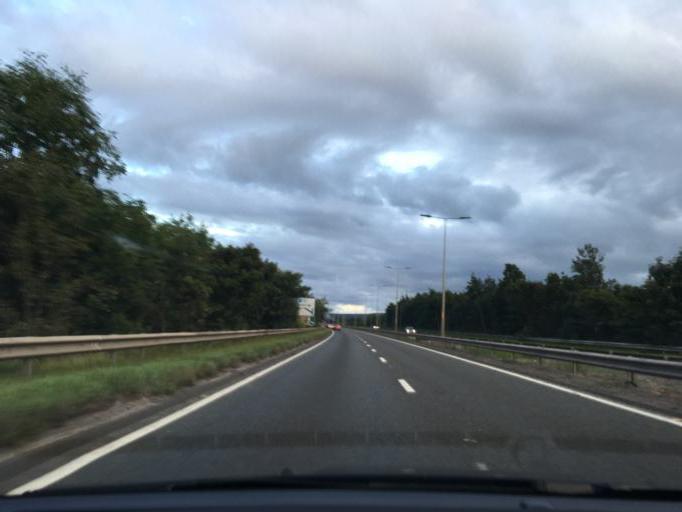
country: GB
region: Scotland
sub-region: Highland
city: Inverness
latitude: 57.4852
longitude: -4.2023
